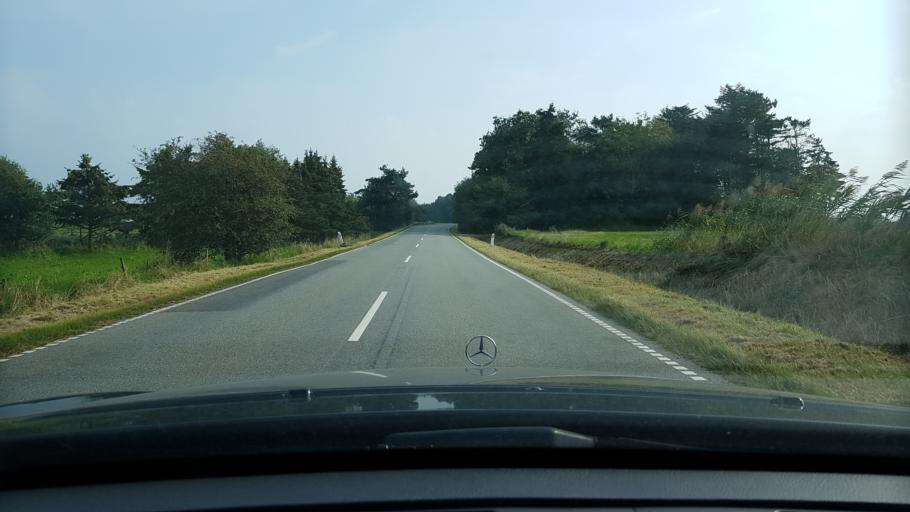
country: DK
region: North Denmark
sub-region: Alborg Kommune
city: Hals
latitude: 56.8942
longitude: 10.2607
